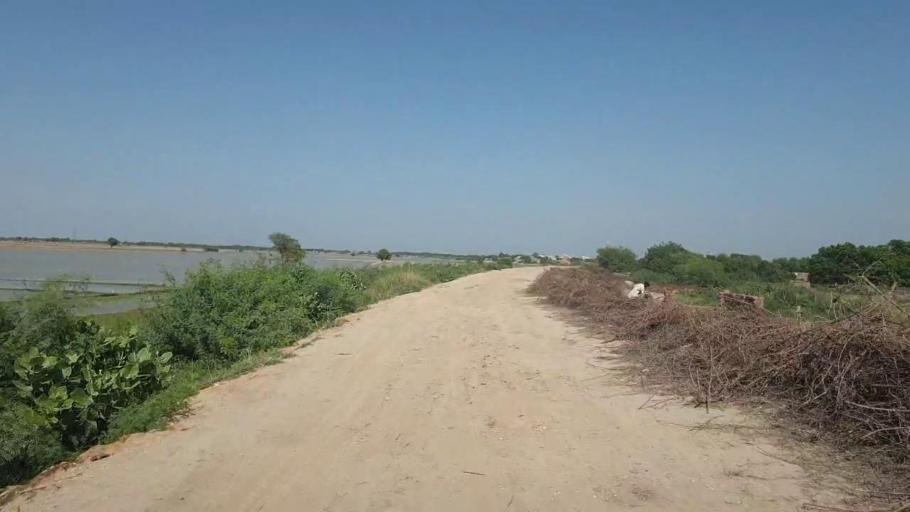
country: PK
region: Sindh
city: Matiari
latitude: 25.6399
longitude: 68.4873
